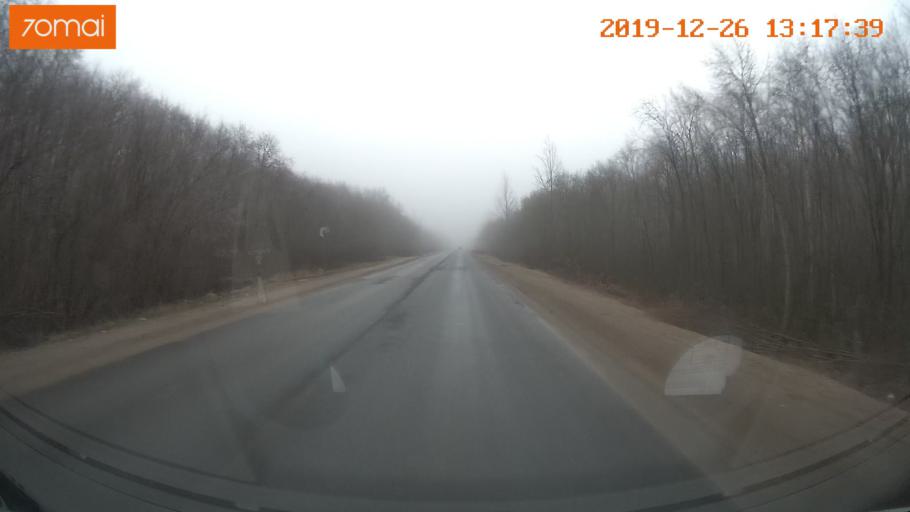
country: RU
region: Vologda
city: Cherepovets
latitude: 58.9670
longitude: 38.1164
